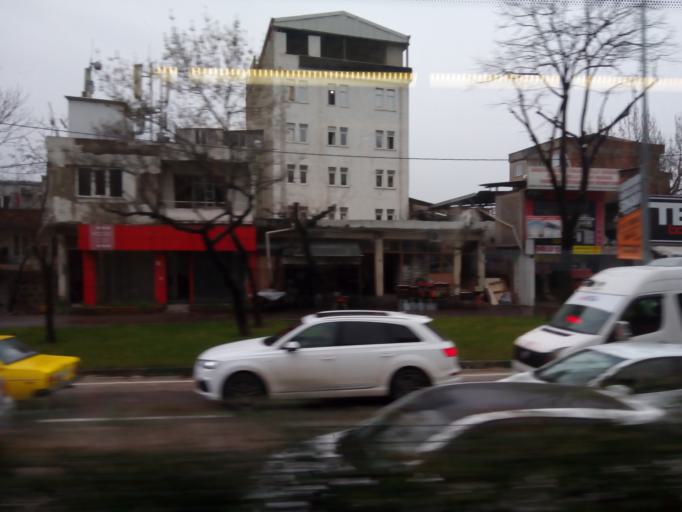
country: TR
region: Bursa
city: Yildirim
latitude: 40.2019
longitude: 29.0358
